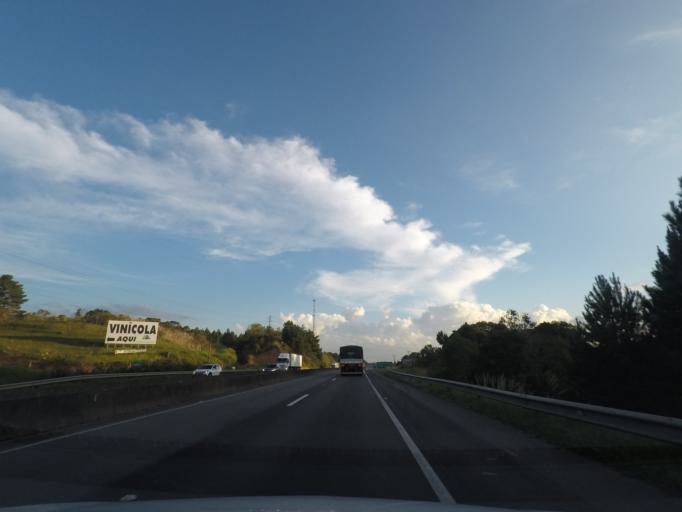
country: BR
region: Parana
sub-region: Campina Grande Do Sul
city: Campina Grande do Sul
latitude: -25.3232
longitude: -49.0250
